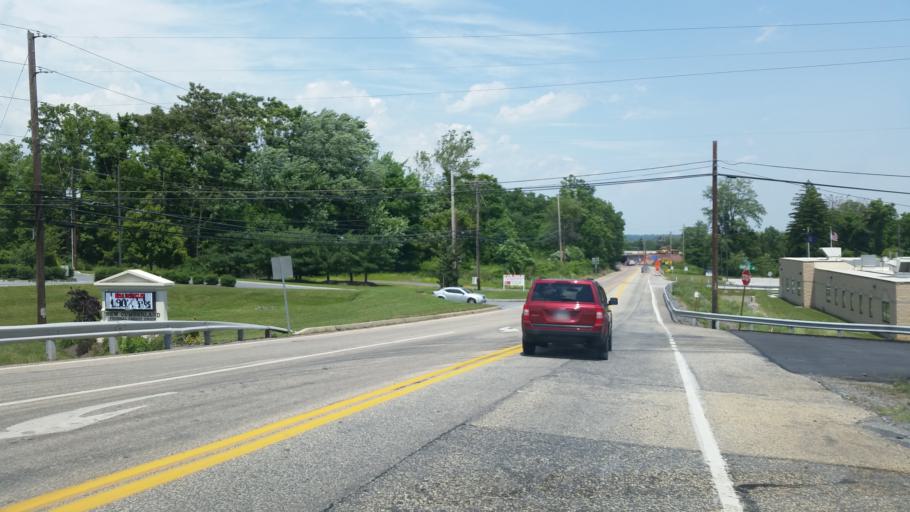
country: US
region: Pennsylvania
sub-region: Cumberland County
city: New Cumberland
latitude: 40.2084
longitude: -76.8727
